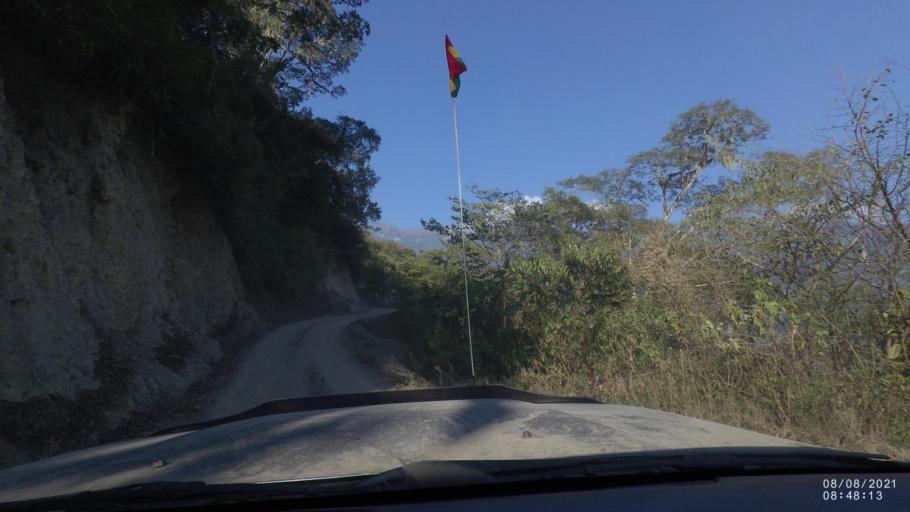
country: BO
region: La Paz
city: Quime
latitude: -16.5302
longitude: -66.7544
